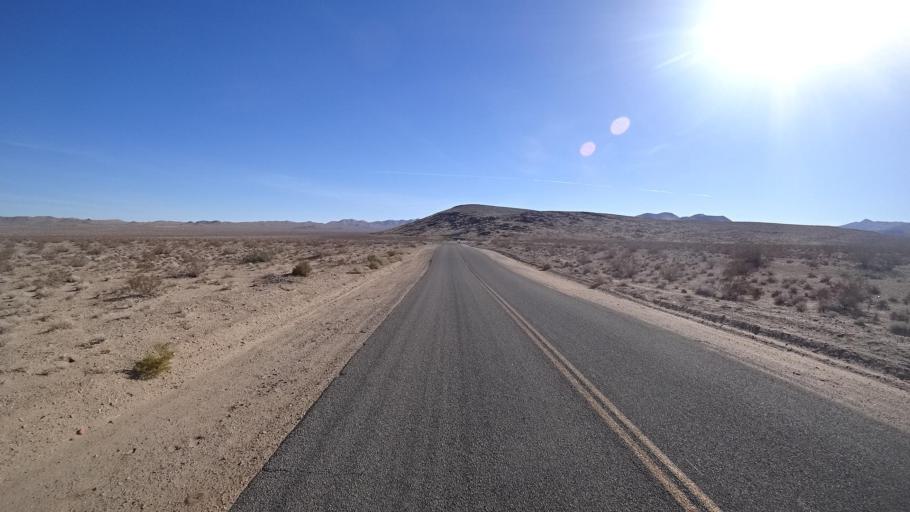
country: US
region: California
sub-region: Kern County
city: China Lake Acres
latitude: 35.5653
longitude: -117.7775
